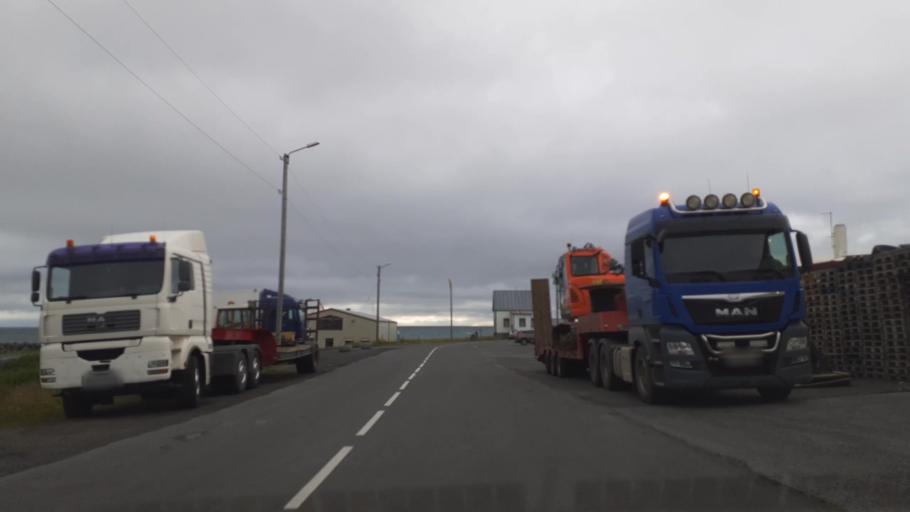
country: IS
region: Northeast
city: Husavik
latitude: 66.3003
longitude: -16.4461
